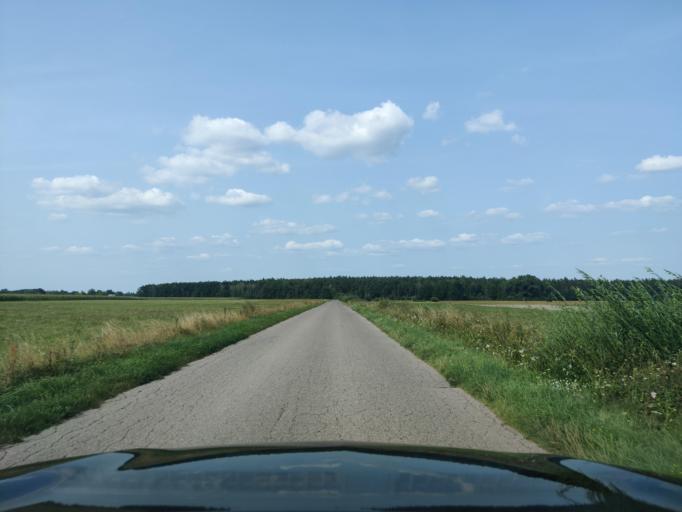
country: PL
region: Masovian Voivodeship
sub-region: Powiat wyszkowski
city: Rzasnik
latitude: 52.7468
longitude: 21.3194
